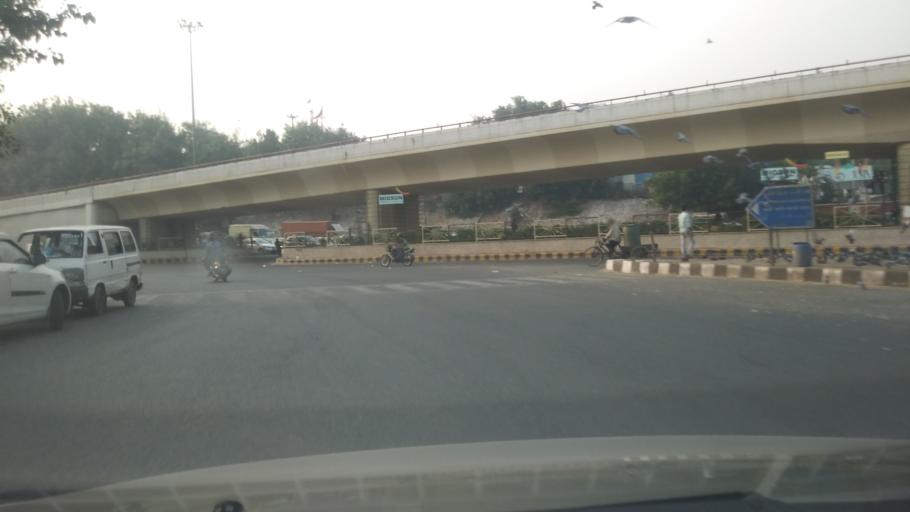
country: IN
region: Uttar Pradesh
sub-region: Gautam Buddha Nagar
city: Noida
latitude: 28.5490
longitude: 77.2623
